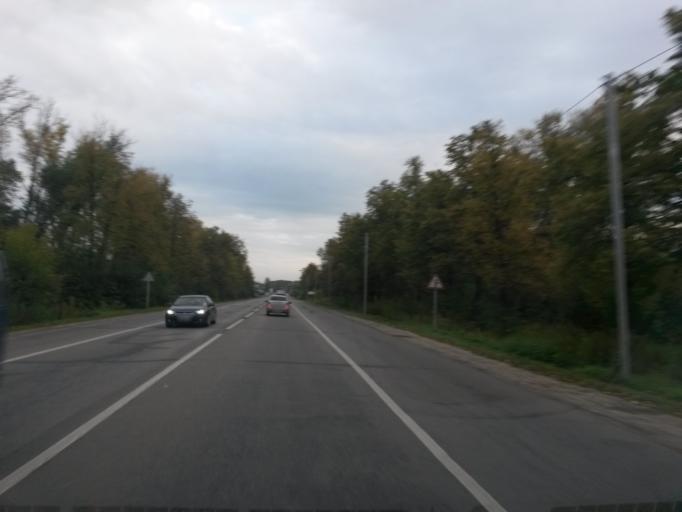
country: RU
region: Moskovskaya
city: Stolbovaya
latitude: 55.2584
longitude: 37.5089
